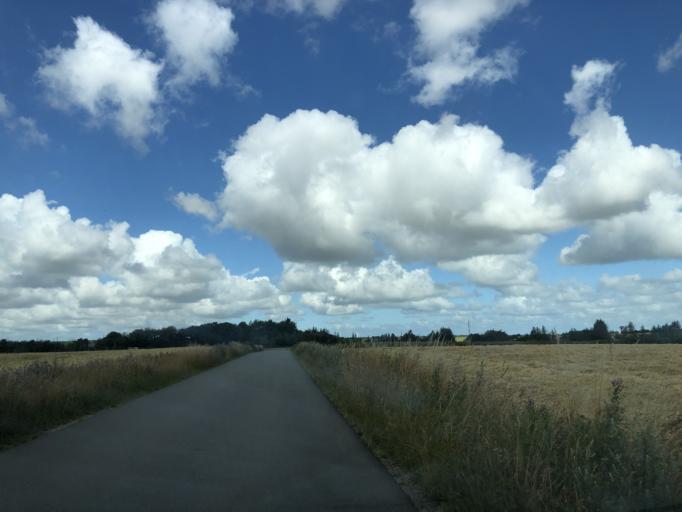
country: DK
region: Central Jutland
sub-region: Struer Kommune
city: Struer
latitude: 56.4766
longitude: 8.5437
